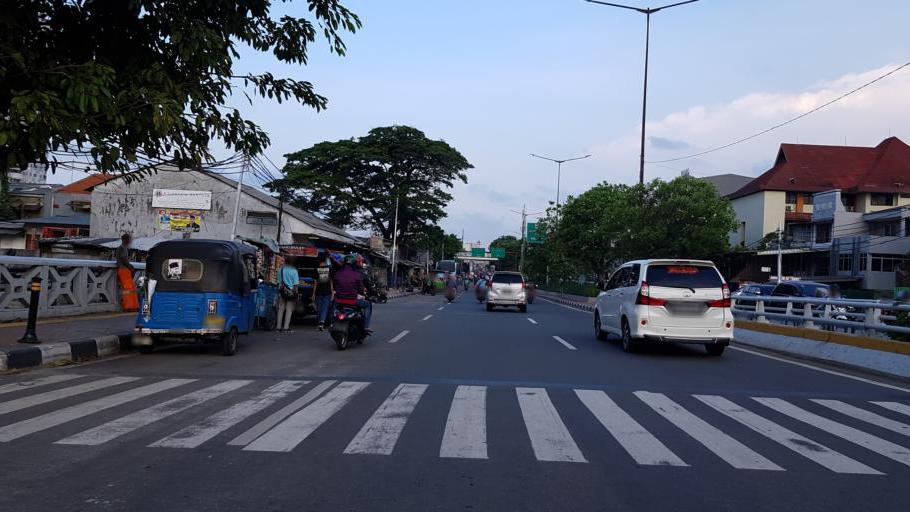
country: ID
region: Jakarta Raya
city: Jakarta
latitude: -6.1431
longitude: 106.7903
